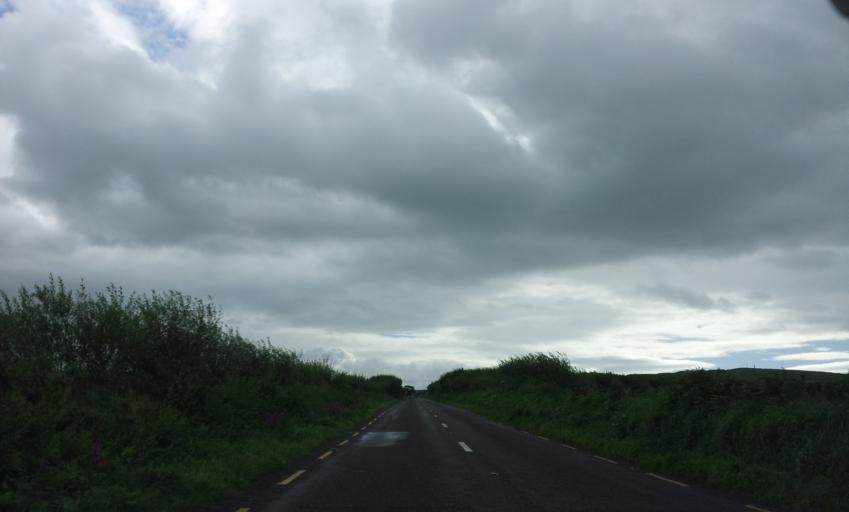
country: IE
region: Munster
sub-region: Ciarrai
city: Dingle
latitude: 52.1406
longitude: -10.1860
